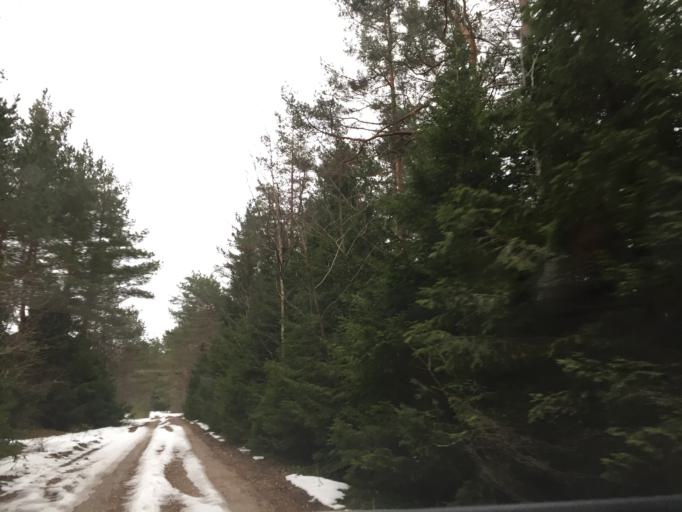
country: EE
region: Saare
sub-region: Kuressaare linn
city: Kuressaare
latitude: 58.4796
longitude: 22.2505
